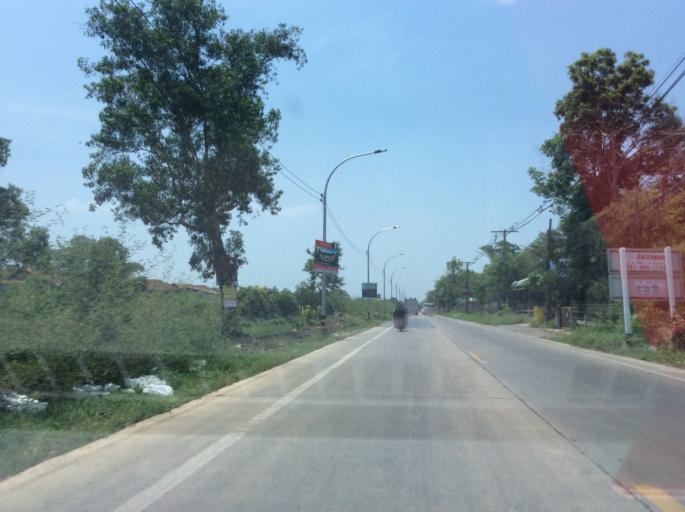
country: TH
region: Pathum Thani
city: Ban Rangsit
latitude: 14.0289
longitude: 100.7787
